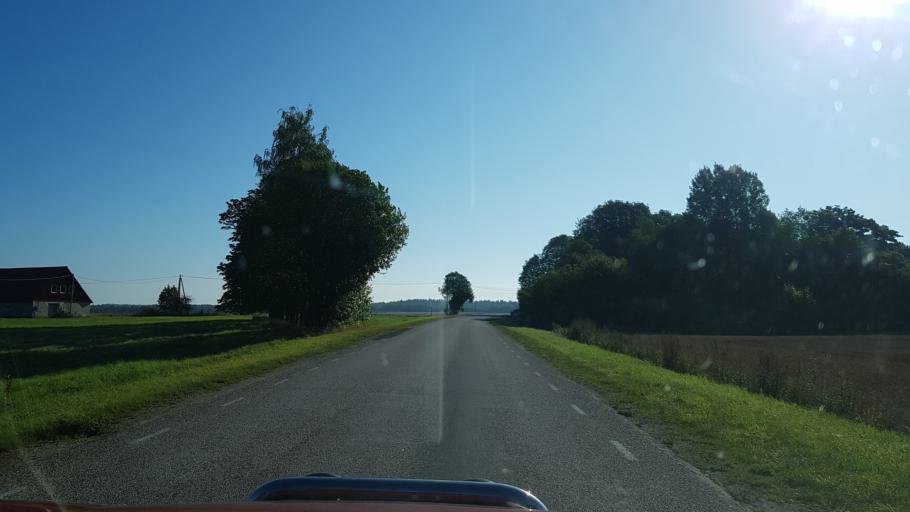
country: EE
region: Jogevamaa
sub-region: Tabivere vald
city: Tabivere
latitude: 58.6821
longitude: 26.6499
